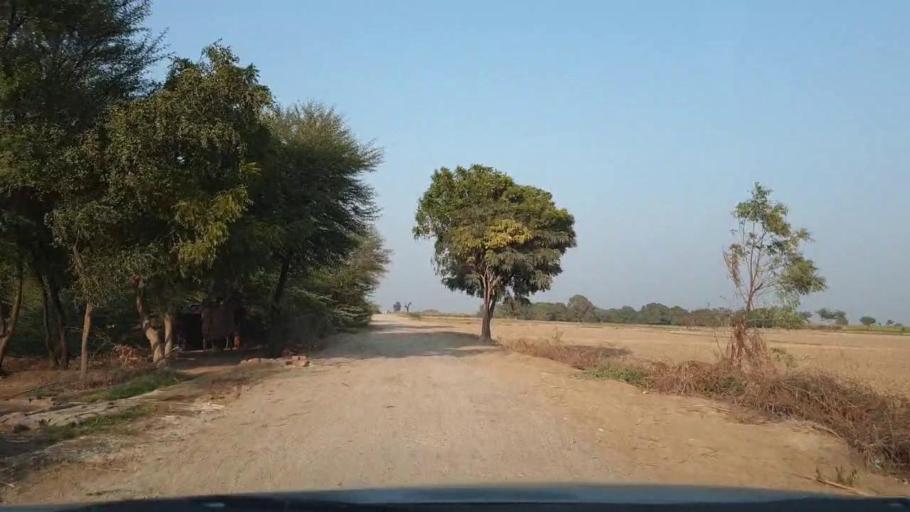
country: PK
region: Sindh
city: Tando Adam
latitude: 25.6957
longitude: 68.6361
